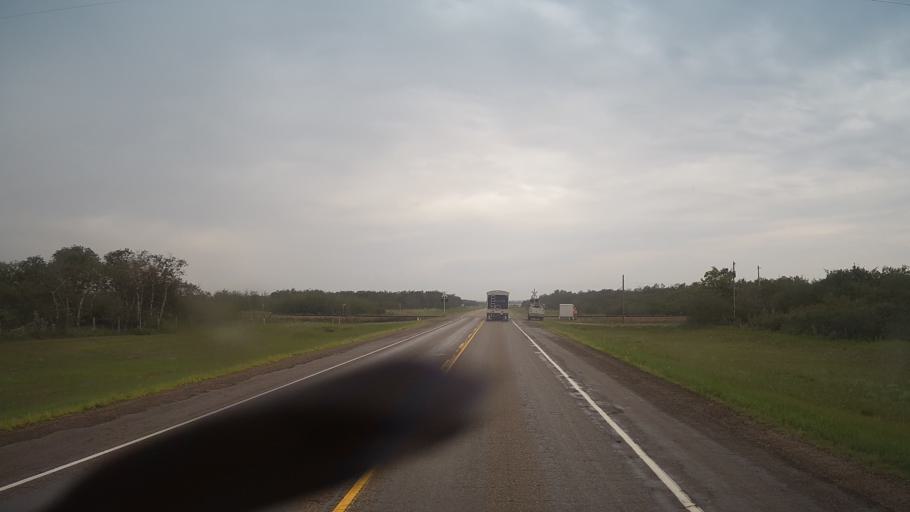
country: CA
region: Saskatchewan
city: Langham
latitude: 52.1294
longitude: -107.0487
